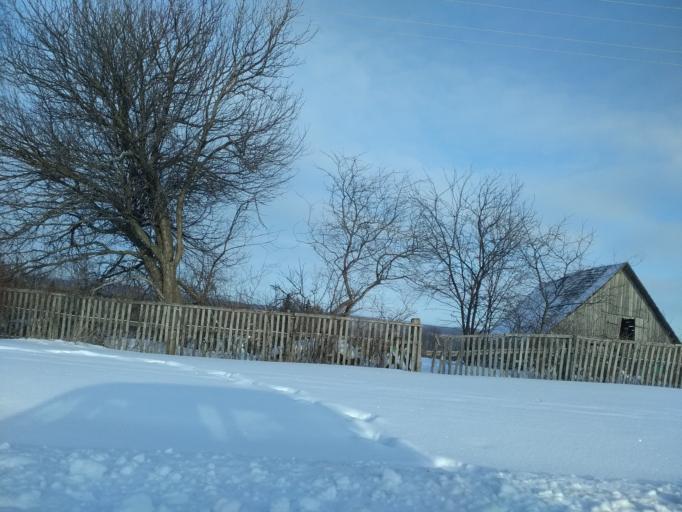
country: RU
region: Bashkortostan
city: Iglino
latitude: 54.6085
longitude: 56.4955
